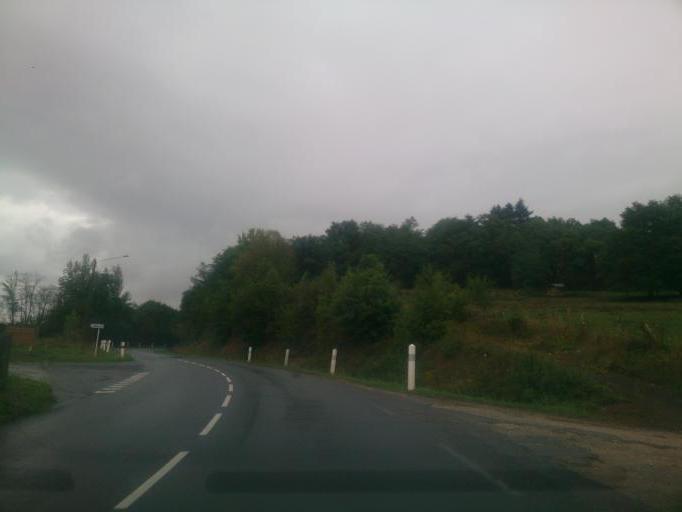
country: FR
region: Limousin
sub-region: Departement de la Correze
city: Malemort-sur-Correze
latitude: 45.1787
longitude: 1.5703
